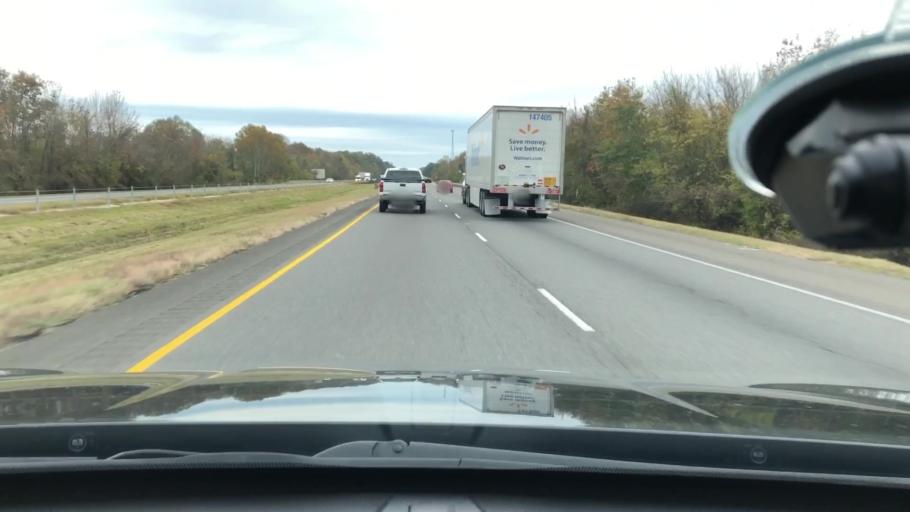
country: US
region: Arkansas
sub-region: Clark County
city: Gurdon
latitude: 34.0088
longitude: -93.1716
